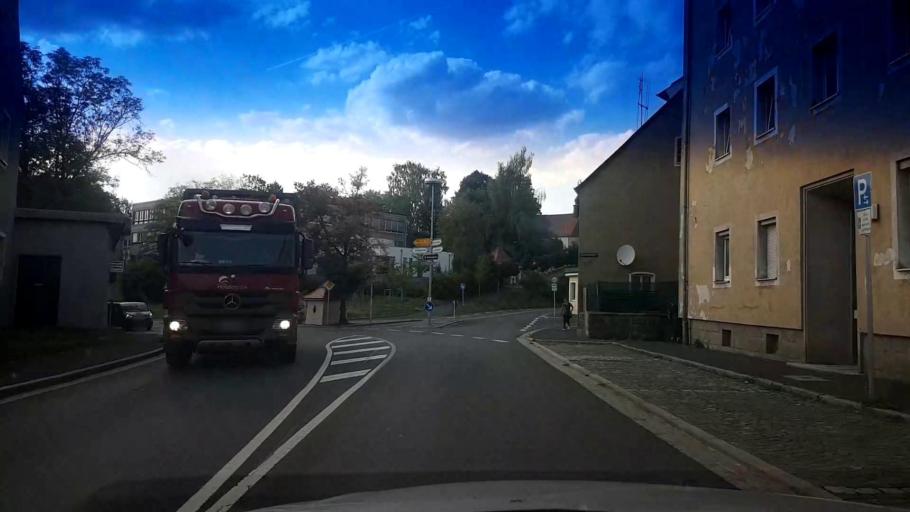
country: DE
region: Bavaria
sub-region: Upper Palatinate
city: Tirschenreuth
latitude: 49.8810
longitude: 12.3400
